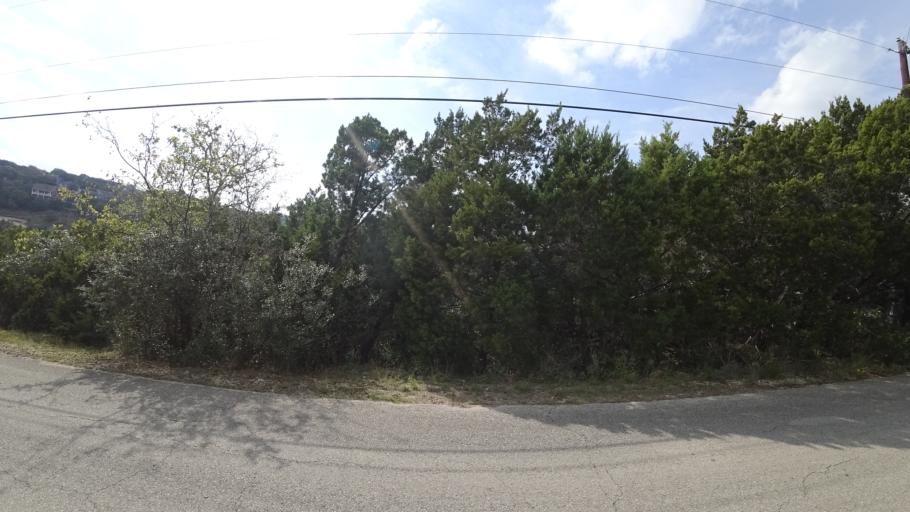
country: US
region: Texas
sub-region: Travis County
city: Hudson Bend
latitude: 30.3794
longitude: -97.9181
